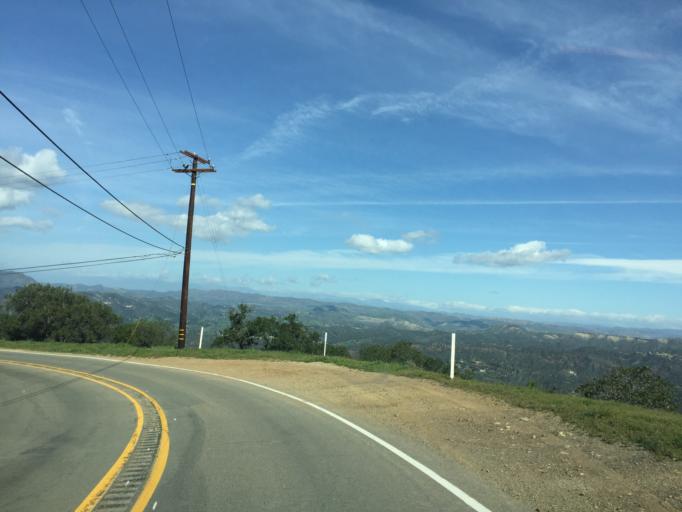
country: US
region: California
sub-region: Los Angeles County
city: Malibu Beach
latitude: 34.0686
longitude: -118.6835
